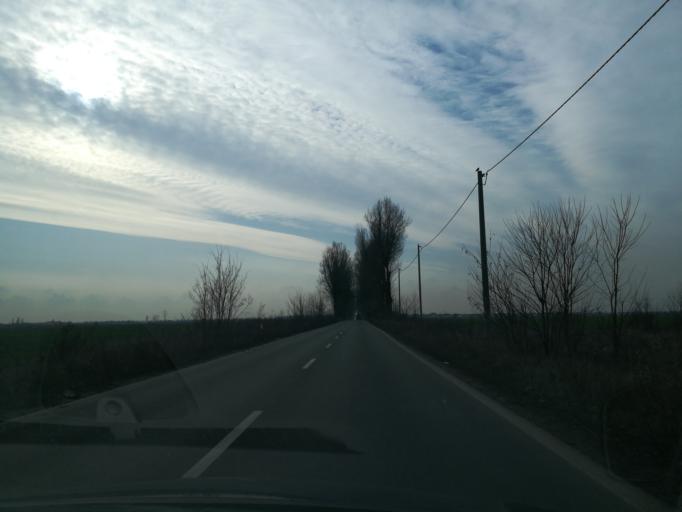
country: RO
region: Ilfov
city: Stefanestii de Jos
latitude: 44.5550
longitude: 26.2183
